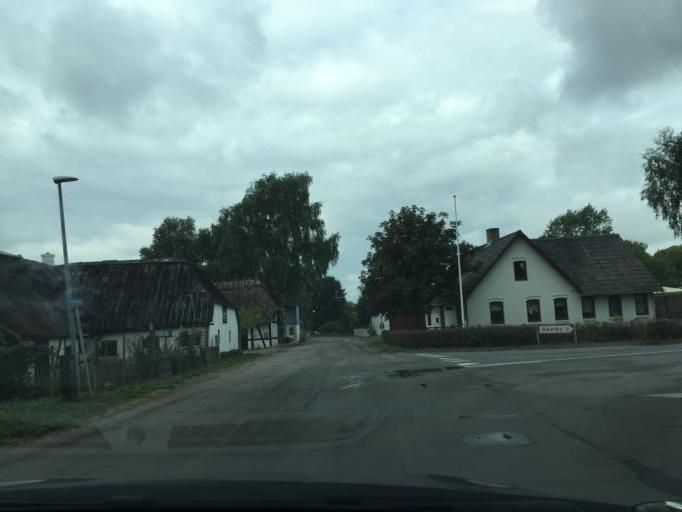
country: DK
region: South Denmark
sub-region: Assens Kommune
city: Harby
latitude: 55.2014
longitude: 10.1164
